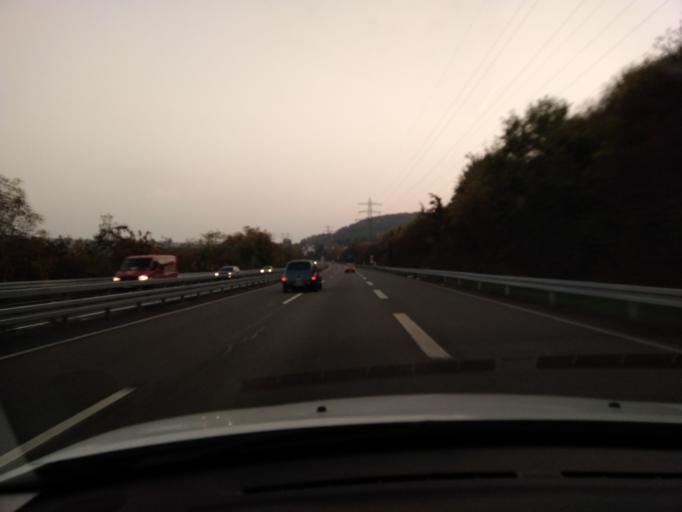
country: DE
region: Saarland
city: Volklingen
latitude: 49.2507
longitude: 6.8333
